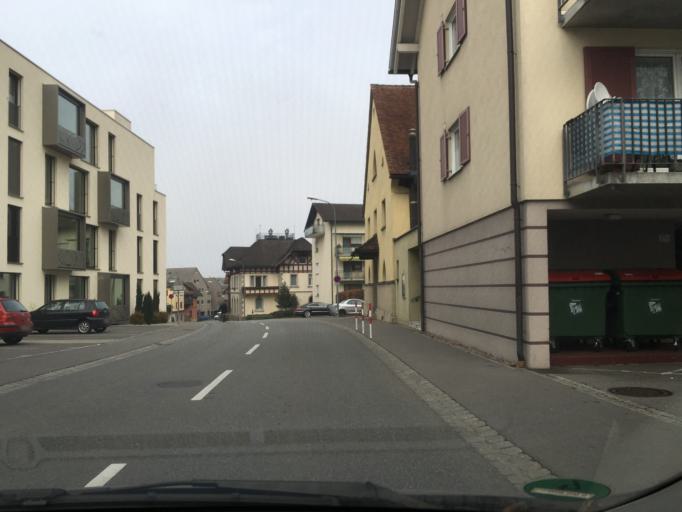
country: AT
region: Vorarlberg
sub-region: Politischer Bezirk Feldkirch
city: Gotzis
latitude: 47.3337
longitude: 9.6479
